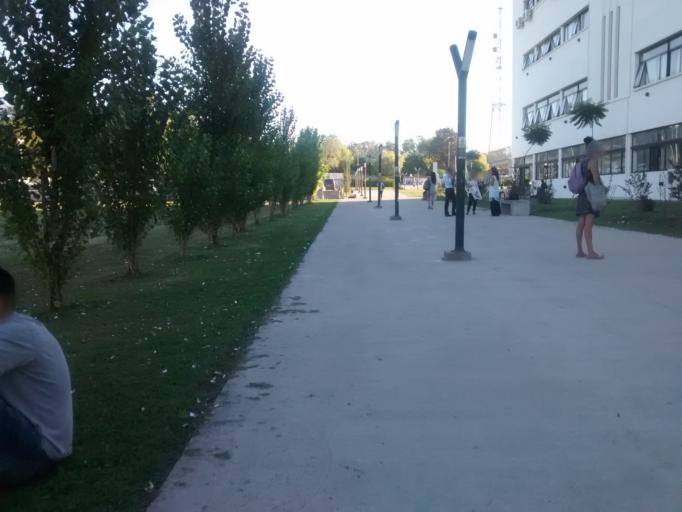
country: AR
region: Buenos Aires
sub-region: Partido de La Plata
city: La Plata
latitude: -34.9009
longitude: -57.9327
